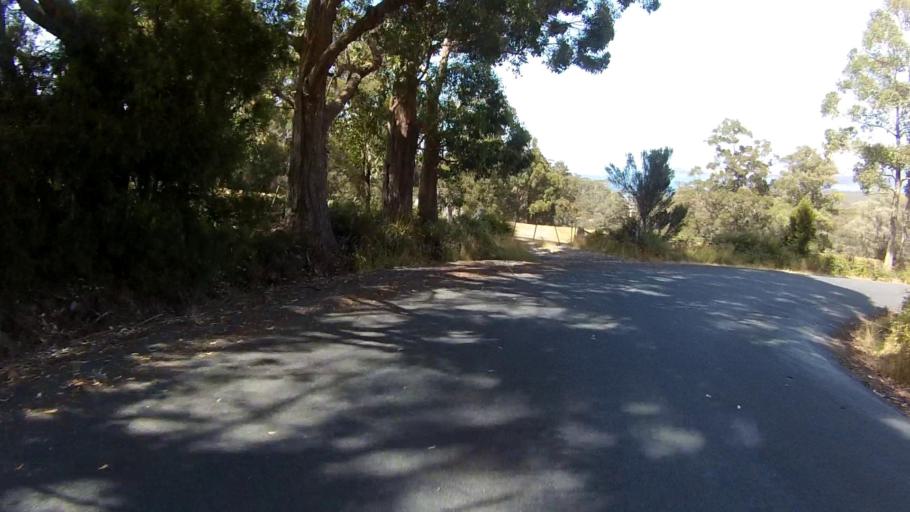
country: AU
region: Tasmania
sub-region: Huon Valley
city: Cygnet
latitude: -43.2319
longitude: 147.1310
